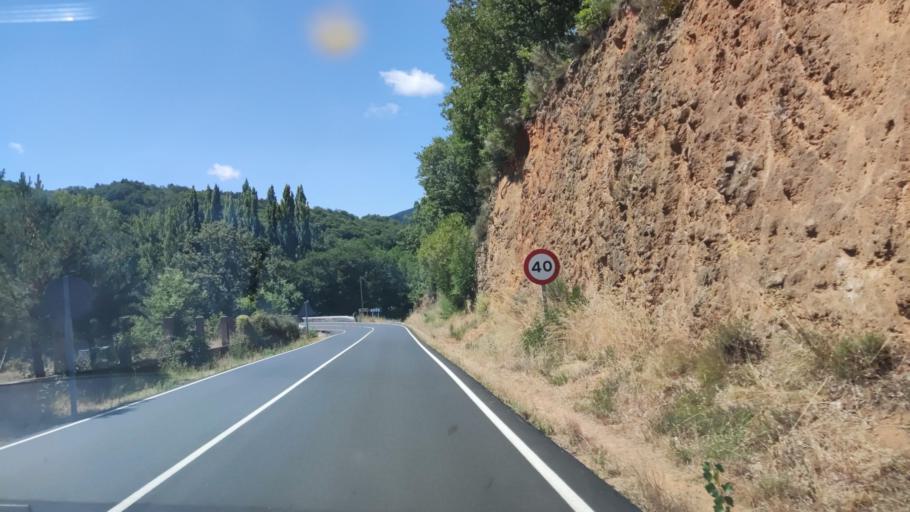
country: ES
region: Castille and Leon
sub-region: Provincia de Salamanca
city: Candelario
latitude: 40.3718
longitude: -5.7514
